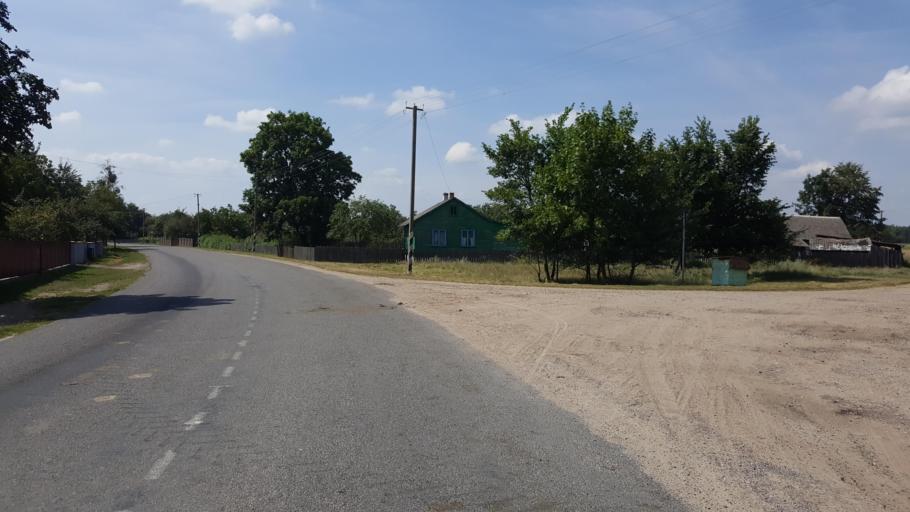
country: PL
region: Podlasie
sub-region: Powiat hajnowski
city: Czeremcha
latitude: 52.5395
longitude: 23.5391
